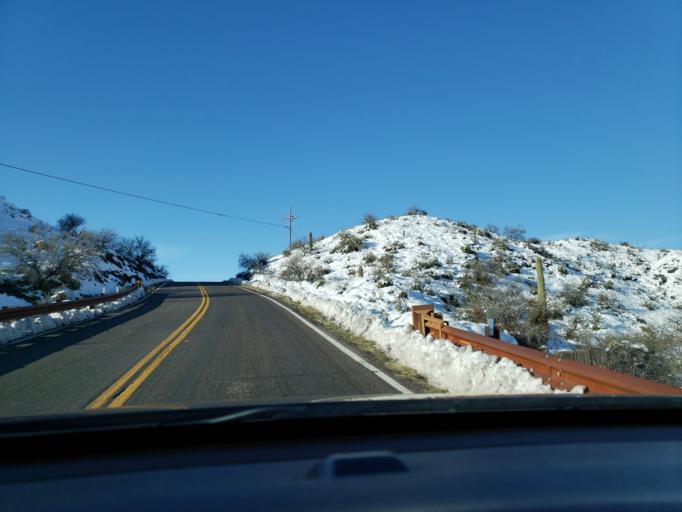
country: US
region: Arizona
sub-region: Maricopa County
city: Carefree
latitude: 33.8867
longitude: -111.8185
